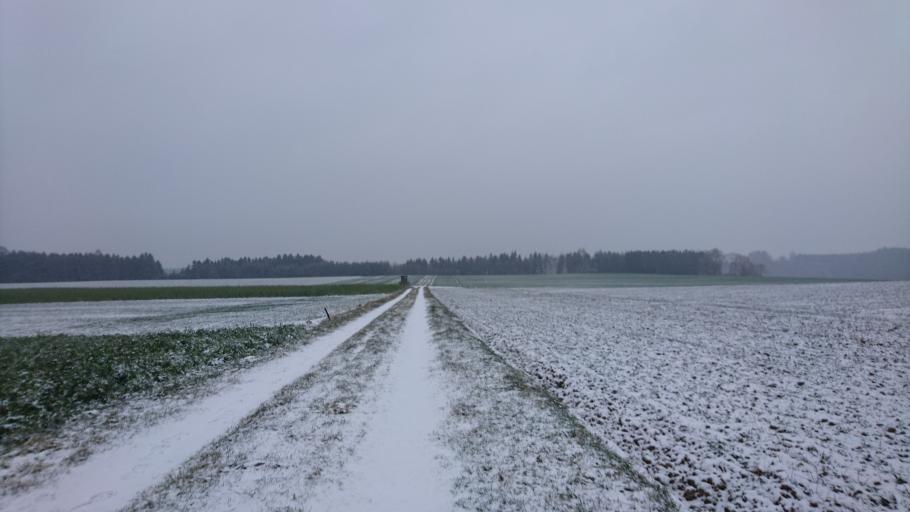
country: DE
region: Bavaria
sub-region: Swabia
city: Altenmunster
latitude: 48.4390
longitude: 10.6155
